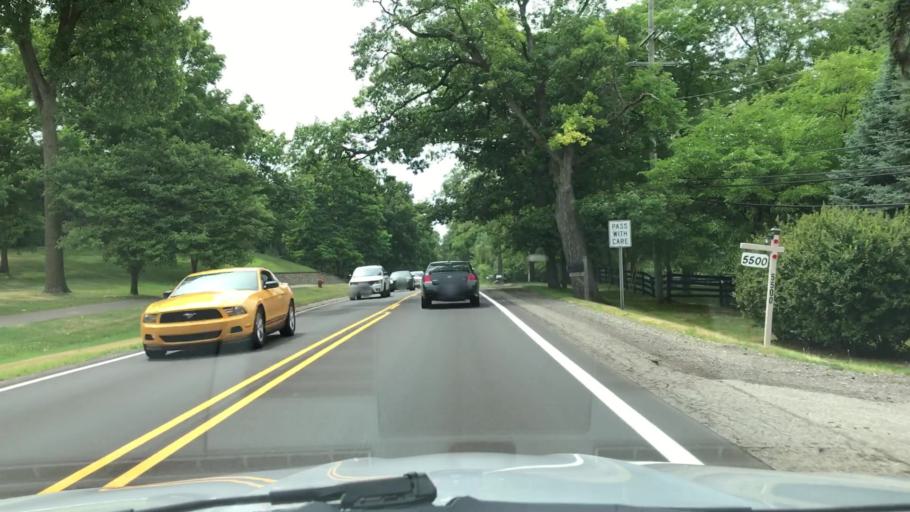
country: US
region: Michigan
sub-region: Oakland County
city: West Bloomfield Township
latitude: 42.5713
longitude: -83.3924
